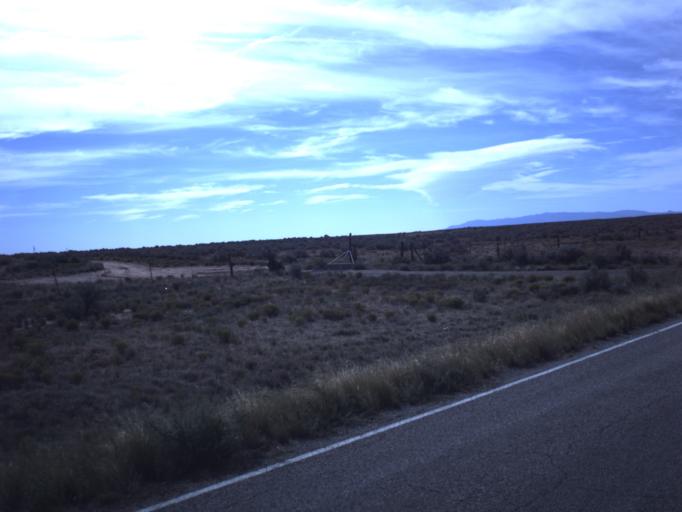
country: US
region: Utah
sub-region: San Juan County
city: Blanding
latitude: 37.3684
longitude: -109.3438
